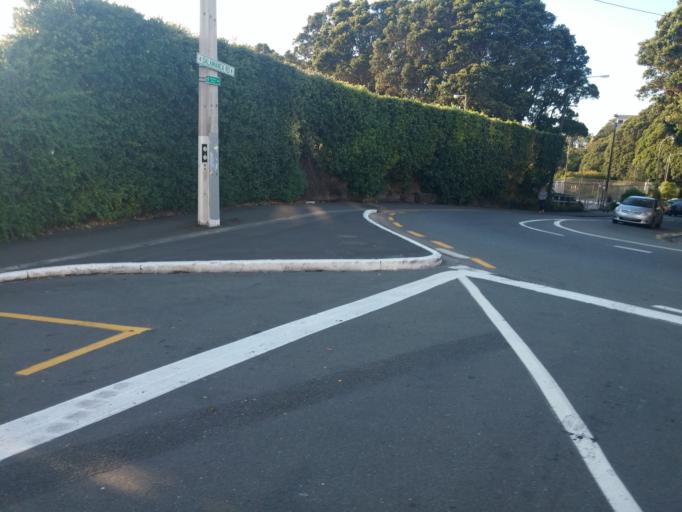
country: NZ
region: Wellington
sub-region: Wellington City
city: Kelburn
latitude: -41.2867
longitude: 174.7691
